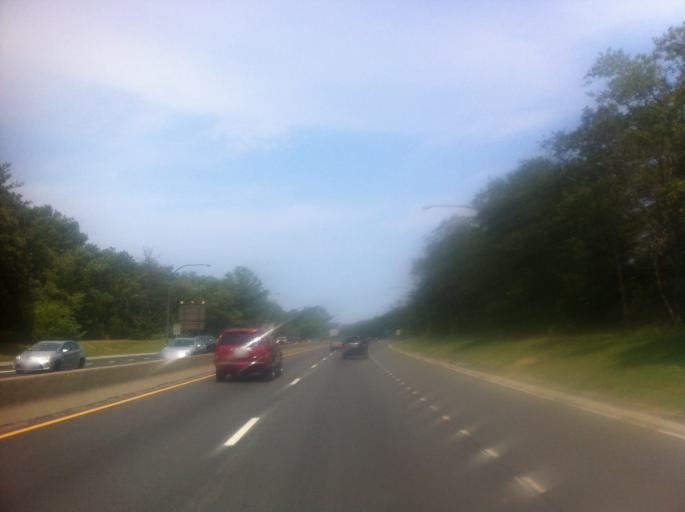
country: US
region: New York
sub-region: Nassau County
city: Jericho
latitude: 40.7842
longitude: -73.5297
